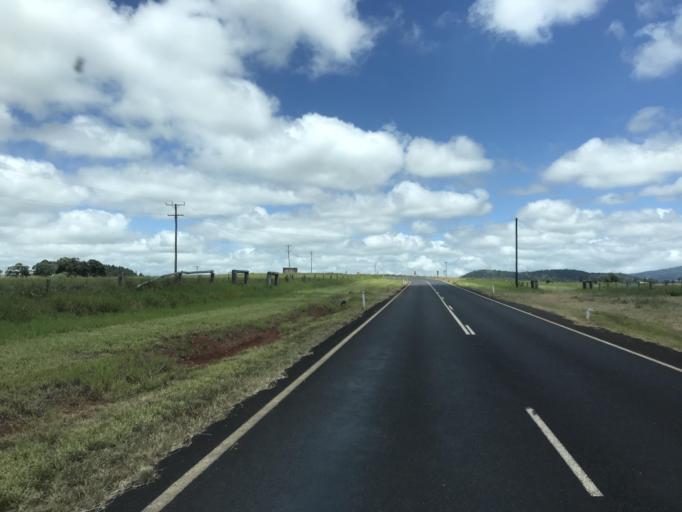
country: AU
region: Queensland
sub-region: Tablelands
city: Ravenshoe
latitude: -17.5087
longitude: 145.4711
